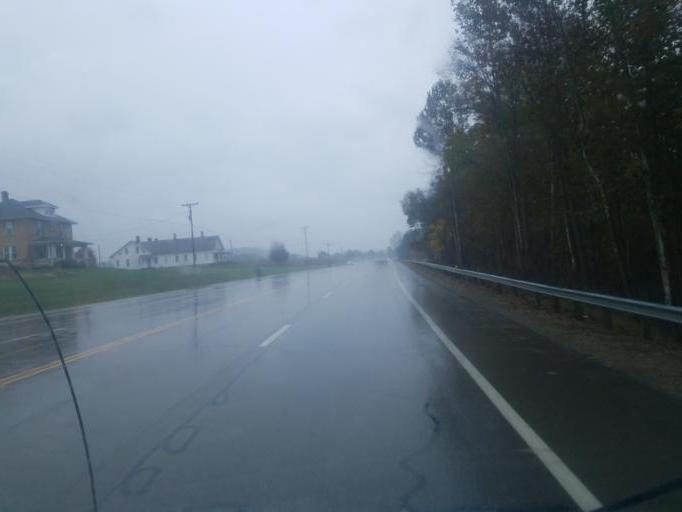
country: US
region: Ohio
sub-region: Muskingum County
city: South Zanesville
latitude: 39.8745
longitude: -81.9283
